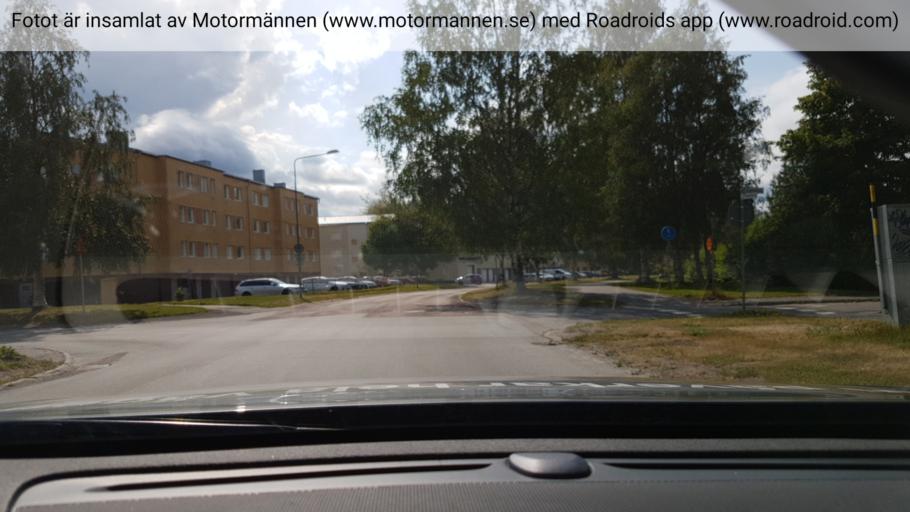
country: SE
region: Vaesterbotten
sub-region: Umea Kommun
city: Umea
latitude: 63.8378
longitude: 20.2364
